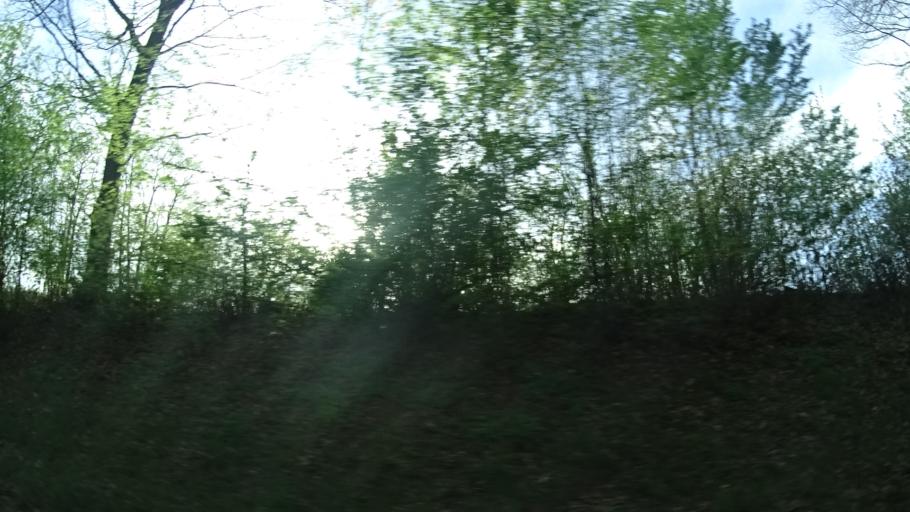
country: DE
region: Baden-Wuerttemberg
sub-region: Karlsruhe Region
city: Limbach
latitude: 49.4883
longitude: 9.2556
